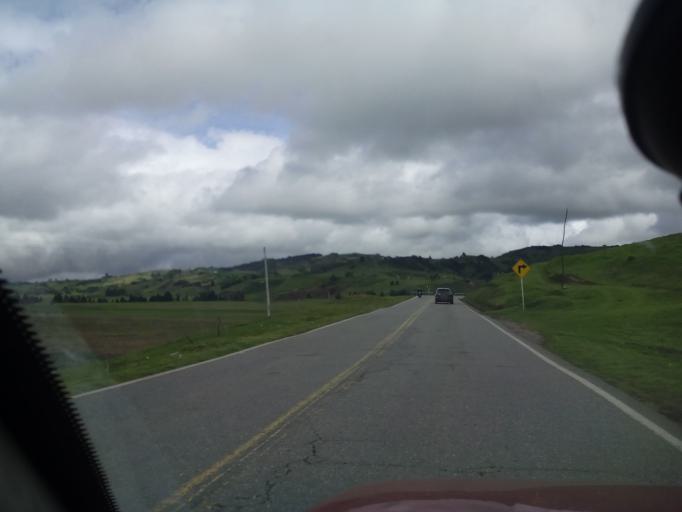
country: CO
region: Boyaca
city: Combita
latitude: 5.6584
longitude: -73.3573
